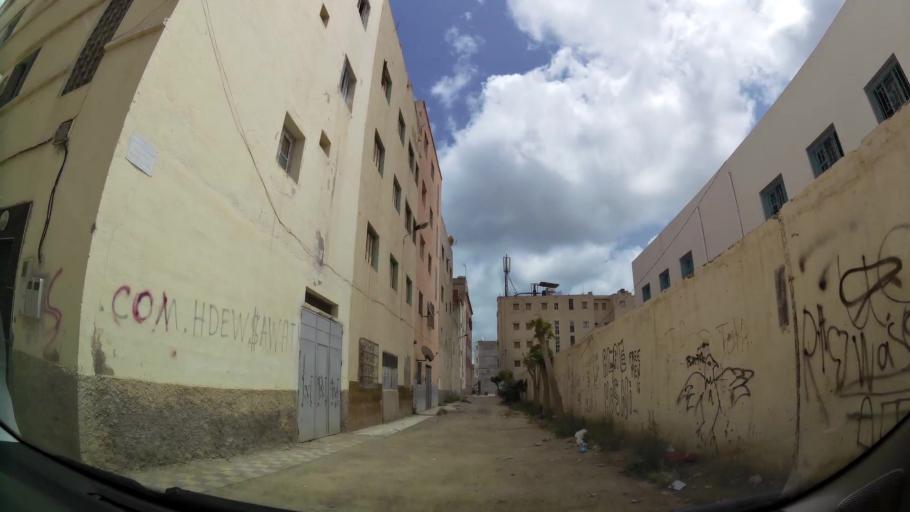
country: MA
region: Oriental
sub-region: Nador
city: Nador
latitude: 35.1748
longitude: -2.9150
